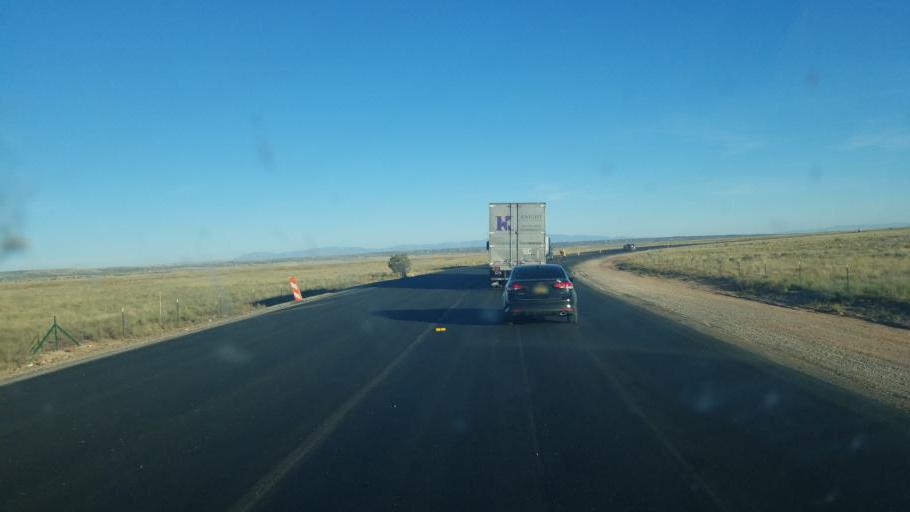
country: US
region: New Mexico
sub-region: Valencia County
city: Los Lunas
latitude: 34.8843
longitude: -107.0637
